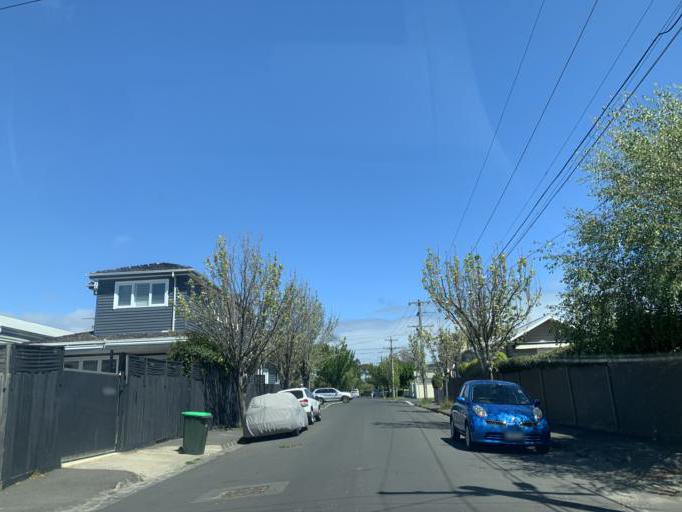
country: AU
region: Victoria
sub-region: Bayside
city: North Brighton
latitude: -37.9103
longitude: 145.0111
